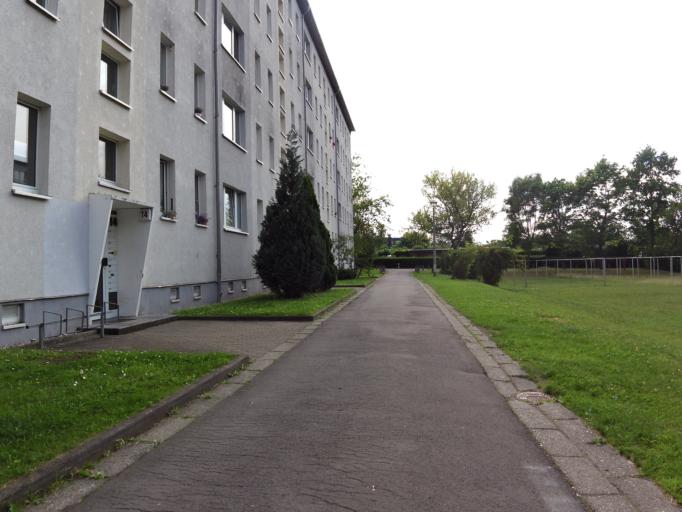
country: DE
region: Saxony
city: Markkleeberg
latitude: 51.3062
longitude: 12.3199
